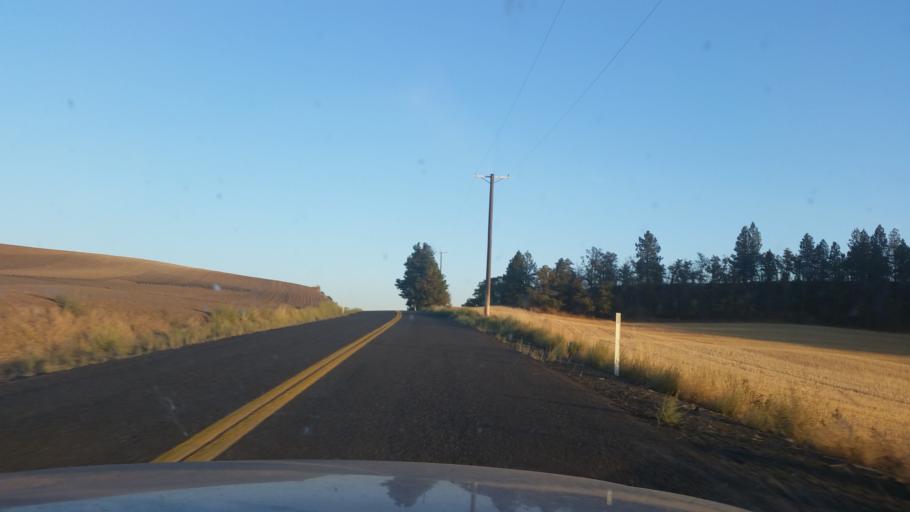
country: US
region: Washington
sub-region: Spokane County
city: Cheney
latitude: 47.5183
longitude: -117.5963
